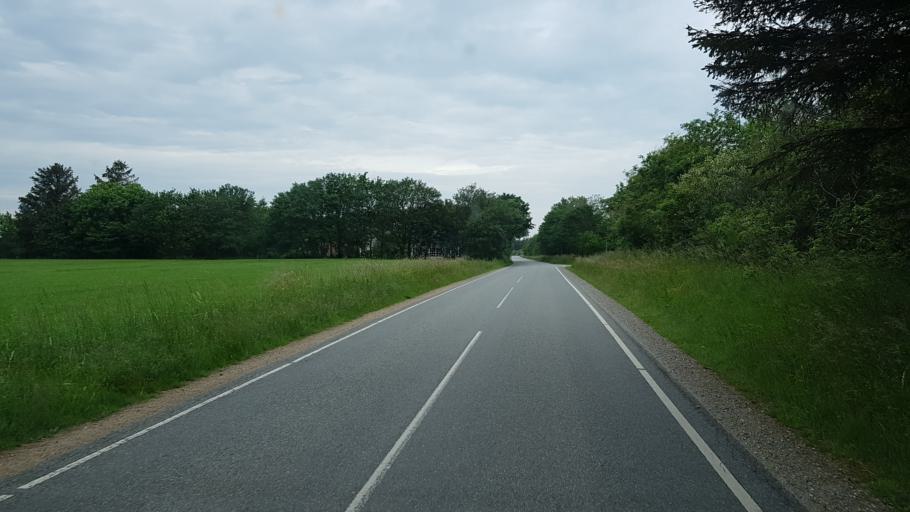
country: DK
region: South Denmark
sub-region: Varde Kommune
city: Oksbol
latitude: 55.6743
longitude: 8.3102
